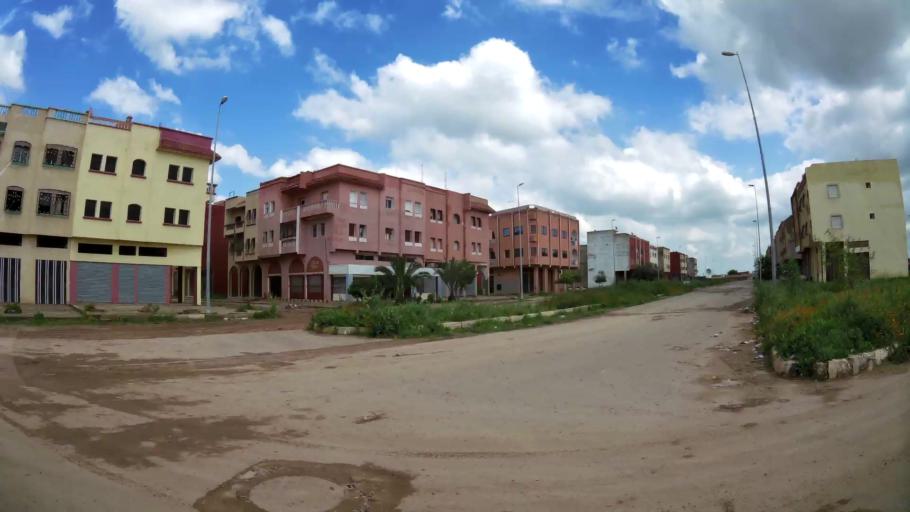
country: MA
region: Grand Casablanca
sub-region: Mediouna
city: Mediouna
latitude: 33.3646
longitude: -7.5335
